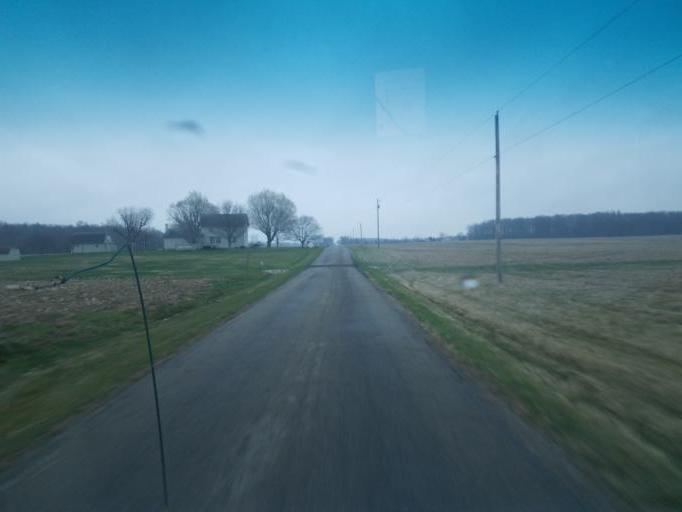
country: US
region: Ohio
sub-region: Defiance County
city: Hicksville
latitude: 41.3391
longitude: -84.7651
